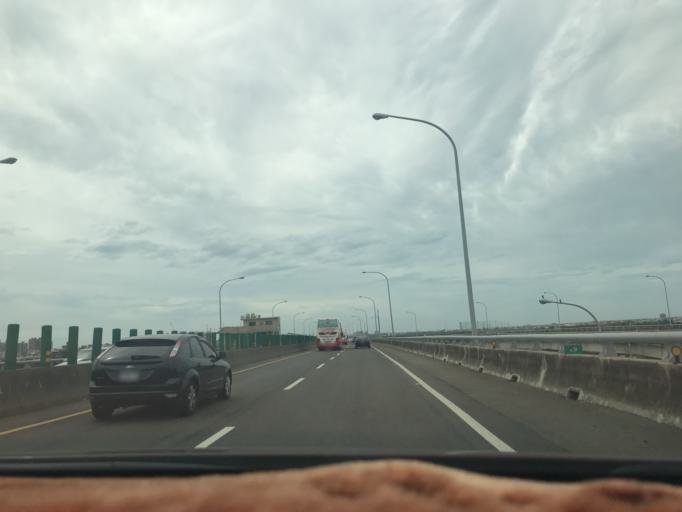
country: TW
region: Taiwan
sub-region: Hsinchu
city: Zhubei
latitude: 24.8199
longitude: 120.9945
